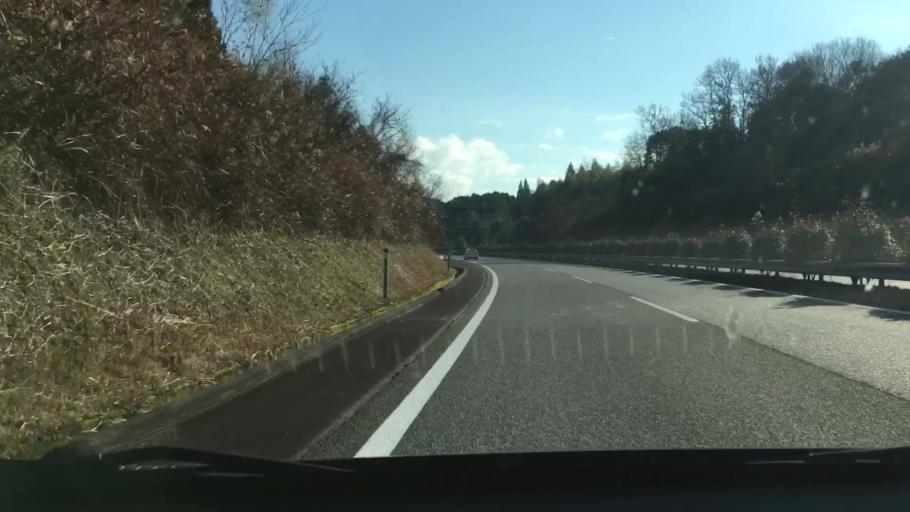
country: JP
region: Kumamoto
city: Hitoyoshi
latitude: 32.1898
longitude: 130.7768
